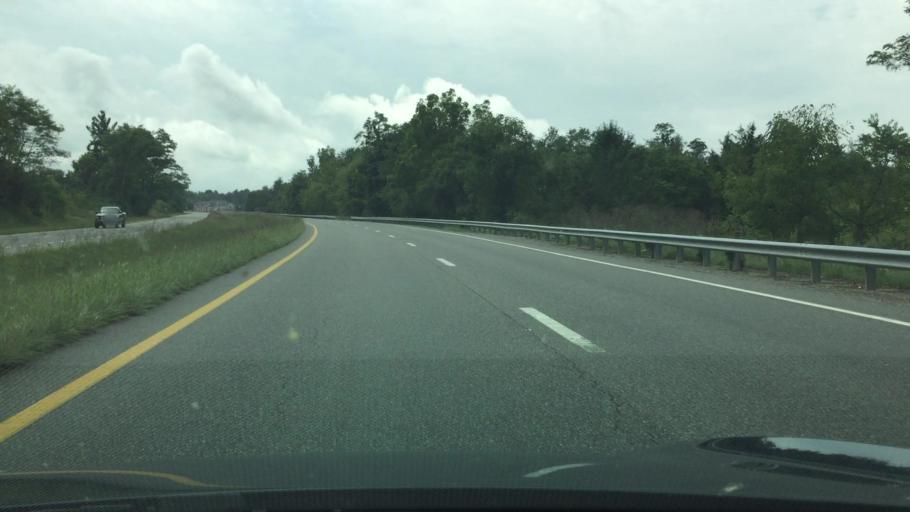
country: US
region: Virginia
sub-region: City of Radford
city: Radford
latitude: 37.1063
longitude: -80.5203
